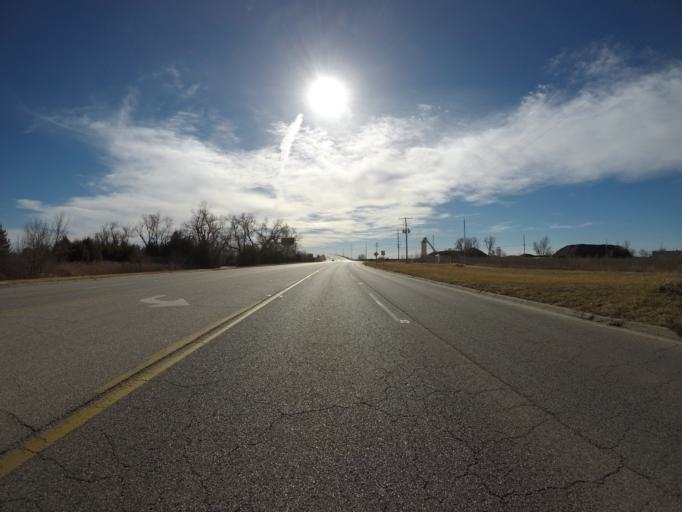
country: US
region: Kansas
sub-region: Reno County
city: Hutchinson
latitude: 38.0529
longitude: -97.8670
